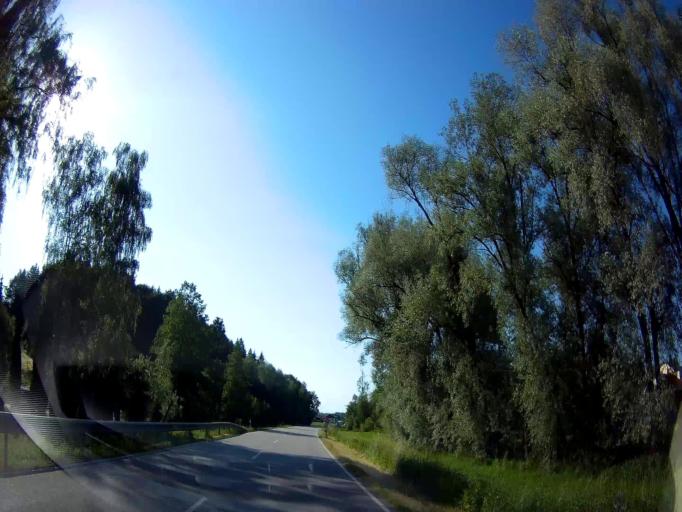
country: DE
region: Bavaria
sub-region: Lower Bavaria
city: Zeilarn
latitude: 48.3039
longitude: 12.8312
